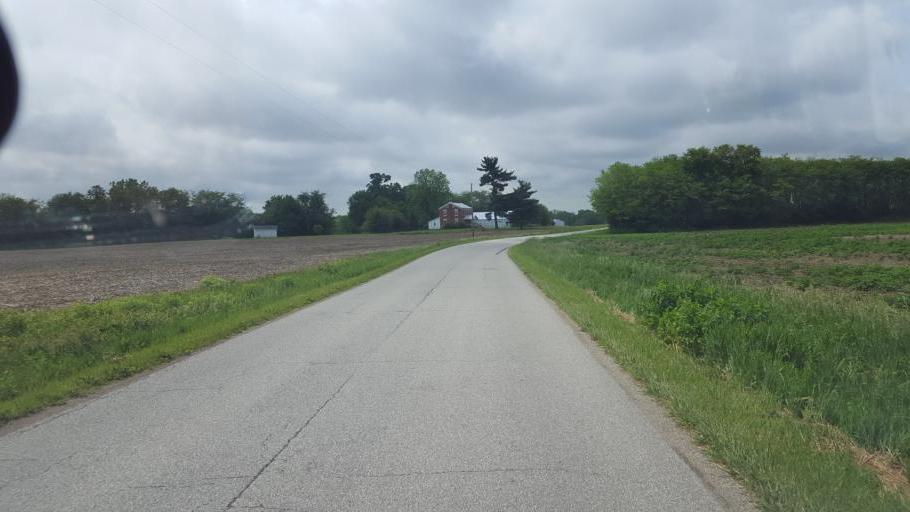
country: US
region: Ohio
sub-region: Delaware County
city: Ashley
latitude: 40.3889
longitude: -82.8778
